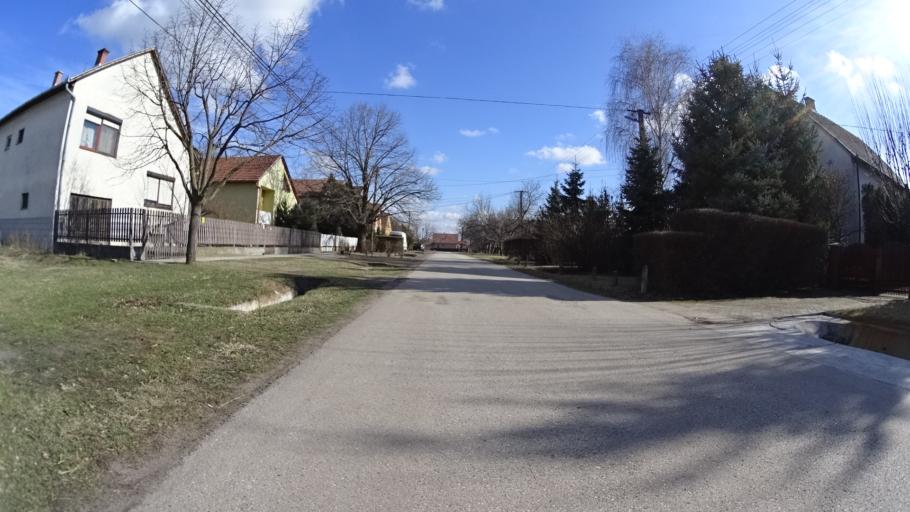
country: HU
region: Bacs-Kiskun
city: Tiszakecske
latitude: 46.9387
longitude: 20.0920
